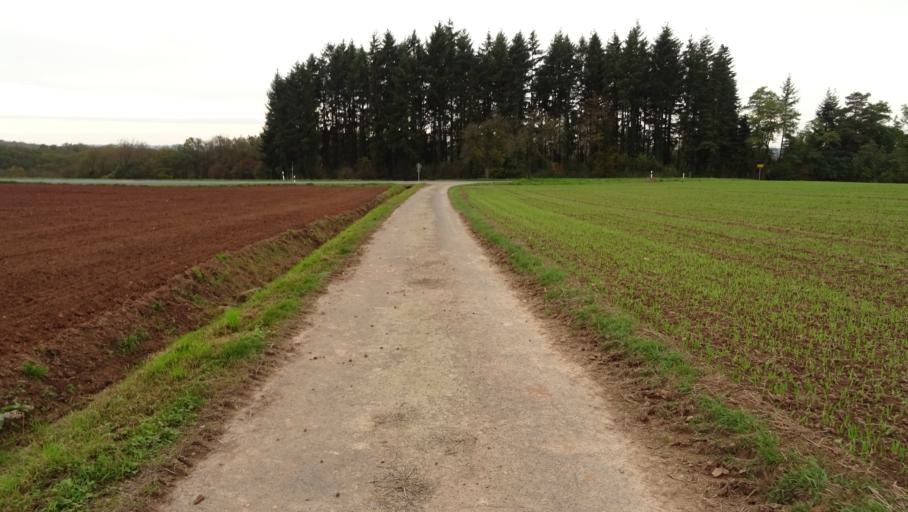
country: DE
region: Baden-Wuerttemberg
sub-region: Karlsruhe Region
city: Neckargerach
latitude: 49.3930
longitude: 9.0857
